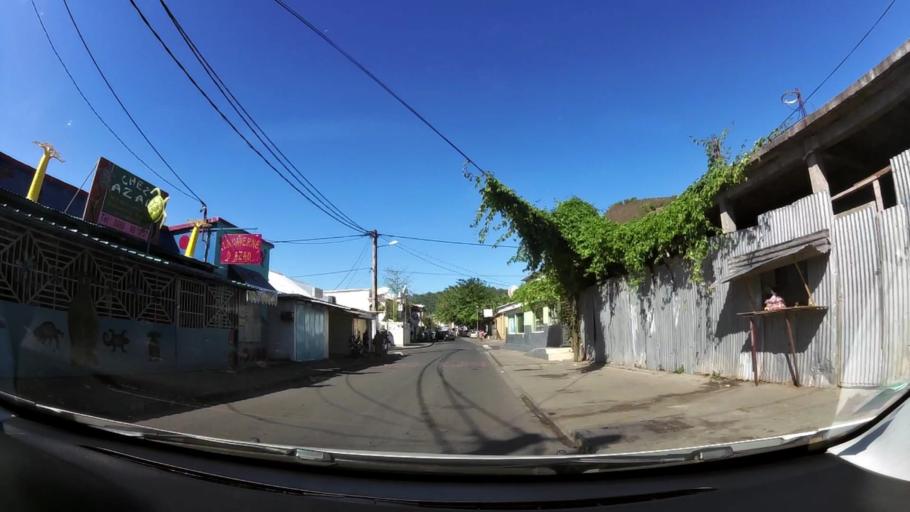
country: YT
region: Pamandzi
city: Pamandzi
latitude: -12.7888
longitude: 45.2714
